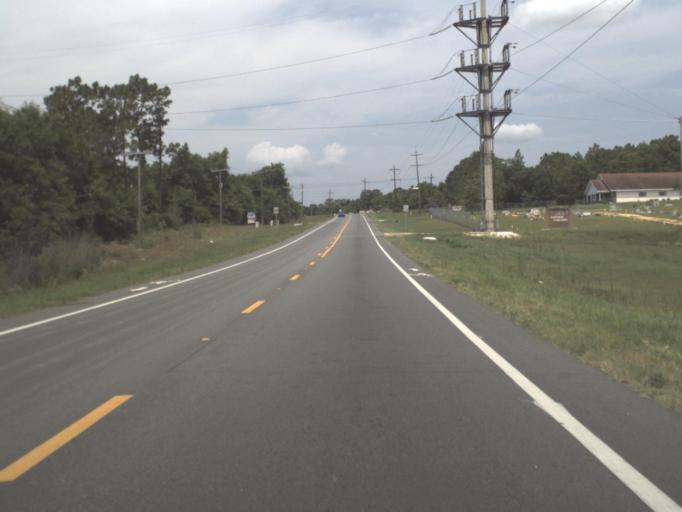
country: US
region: Florida
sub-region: Putnam County
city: Interlachen
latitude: 29.6259
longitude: -81.8994
